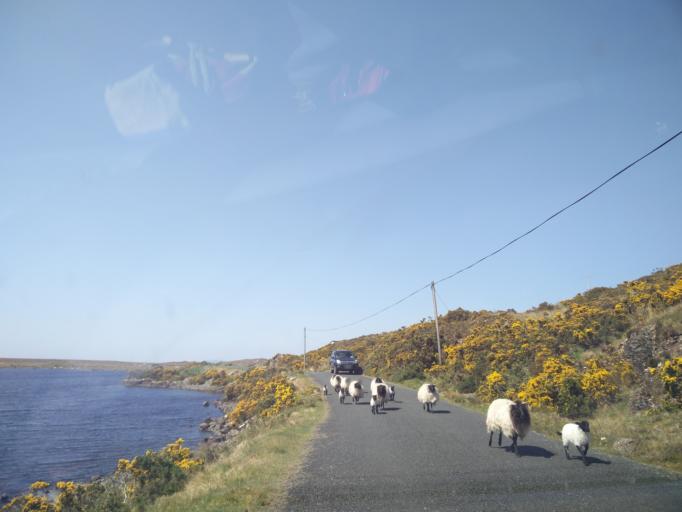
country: IE
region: Connaught
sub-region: County Galway
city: Clifden
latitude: 53.6010
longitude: -9.8553
